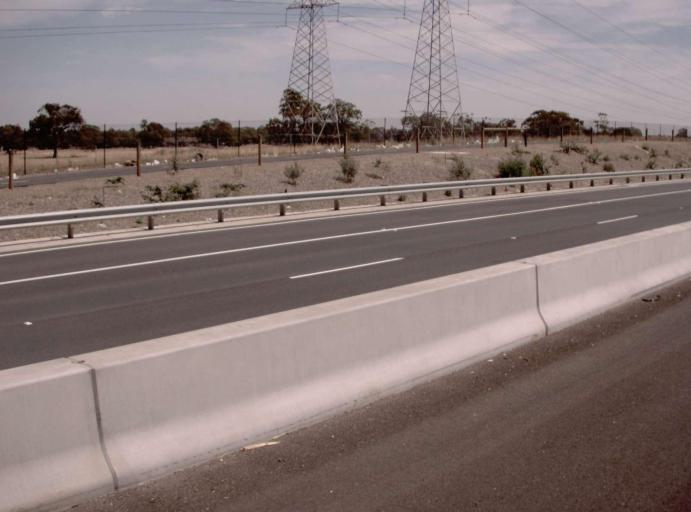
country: AU
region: Victoria
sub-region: Hume
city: Campbellfield
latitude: -37.6922
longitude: 144.9540
